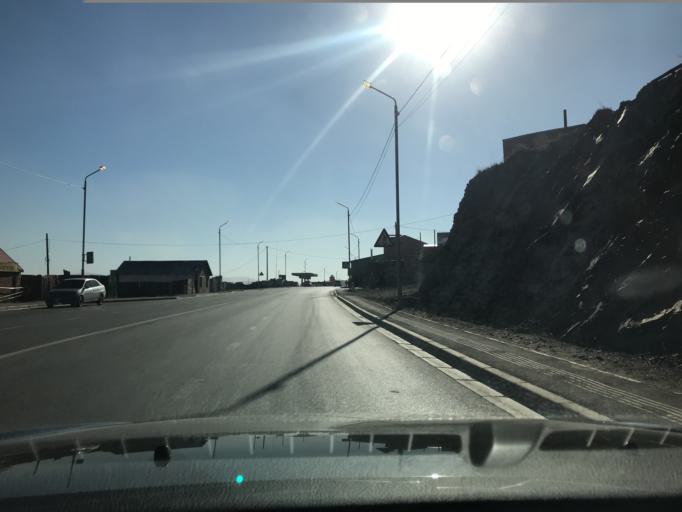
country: MN
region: Ulaanbaatar
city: Ulaanbaatar
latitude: 47.9843
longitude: 106.9244
